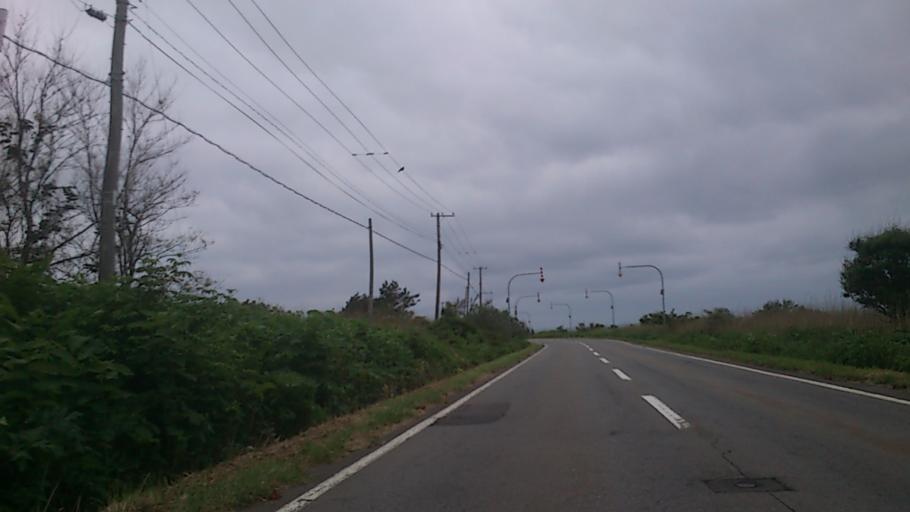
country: JP
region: Hokkaido
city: Kamiiso
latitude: 41.7180
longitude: 140.0346
